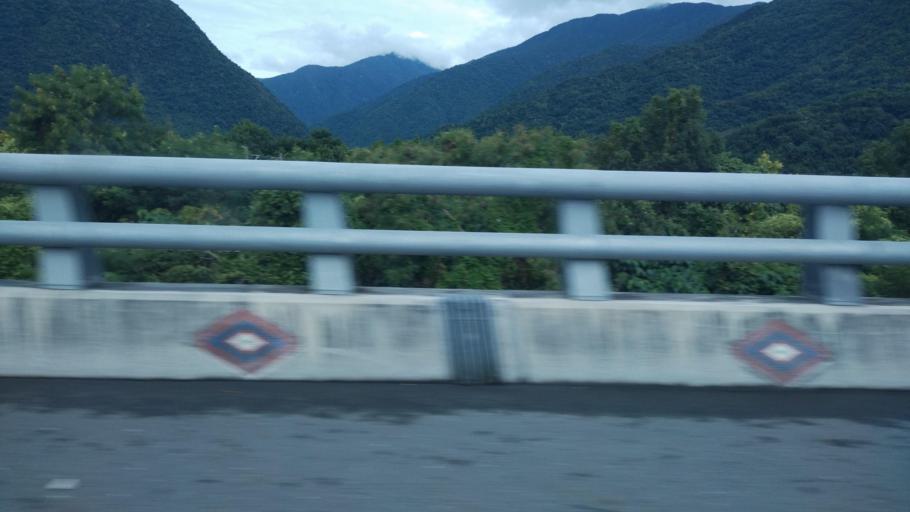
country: TW
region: Taiwan
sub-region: Yilan
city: Yilan
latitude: 24.4635
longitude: 121.7904
